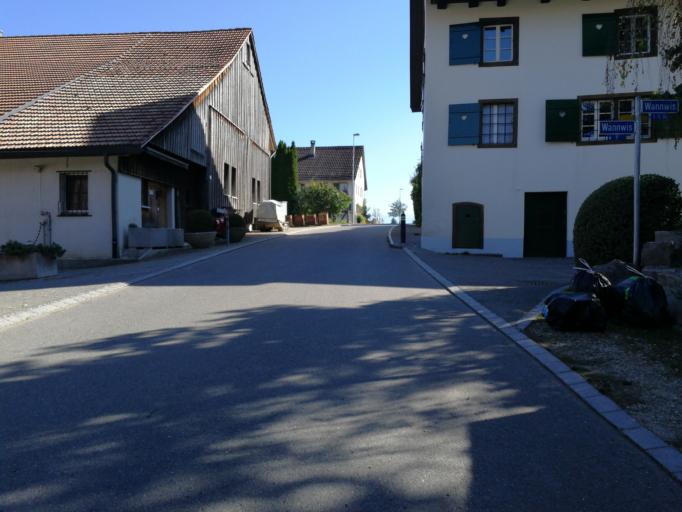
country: CH
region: Zurich
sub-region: Bezirk Uster
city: Aesch
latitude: 47.3223
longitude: 8.6687
